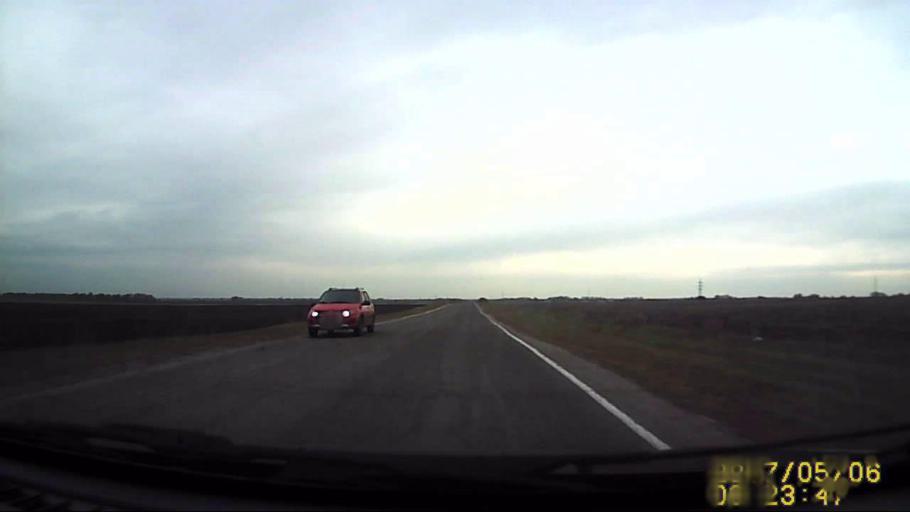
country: RU
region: Ulyanovsk
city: Cherdakly
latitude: 54.3771
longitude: 48.7961
